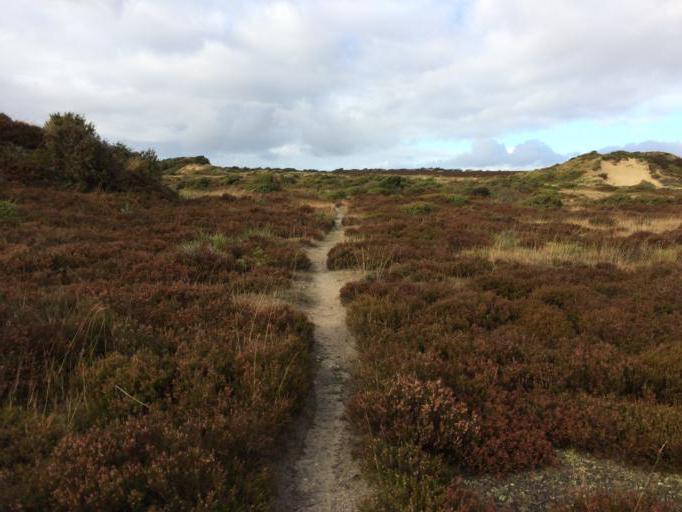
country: DK
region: Central Jutland
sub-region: Holstebro Kommune
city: Ulfborg
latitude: 56.2554
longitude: 8.4124
